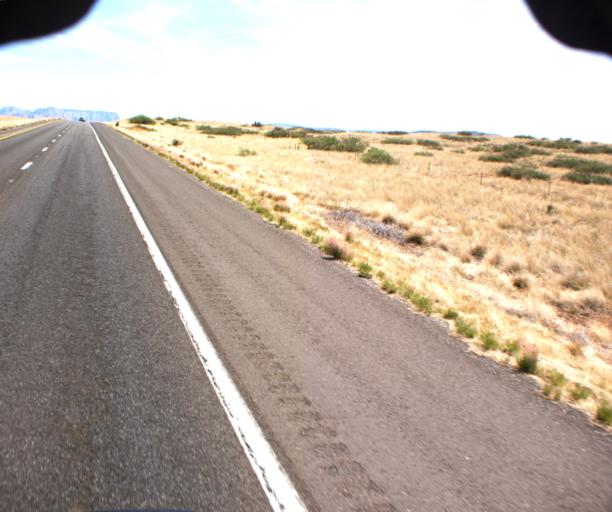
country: US
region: Arizona
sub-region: Yavapai County
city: Cornville
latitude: 34.7582
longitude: -111.9511
